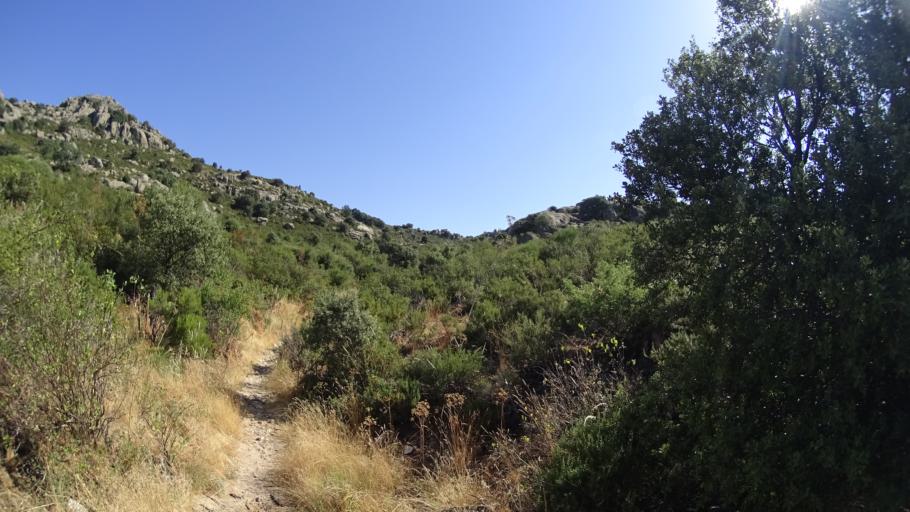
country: ES
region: Madrid
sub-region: Provincia de Madrid
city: Hoyo de Manzanares
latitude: 40.6436
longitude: -3.9359
